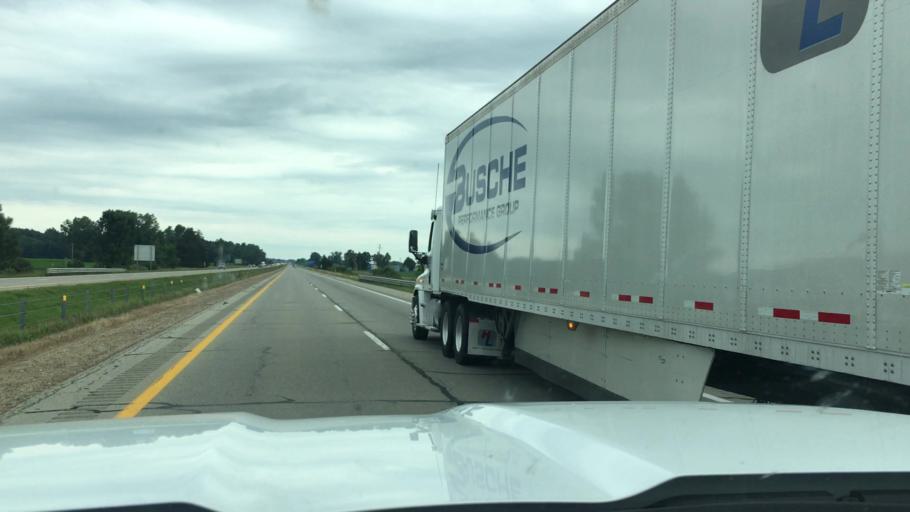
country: US
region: Michigan
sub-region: Allegan County
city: Wayland
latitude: 42.6557
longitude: -85.6621
